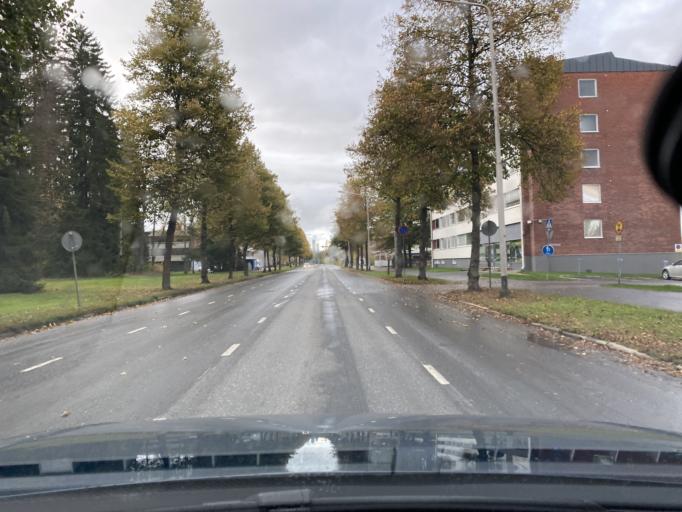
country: FI
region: Haeme
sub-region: Forssa
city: Forssa
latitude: 60.8186
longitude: 23.6105
